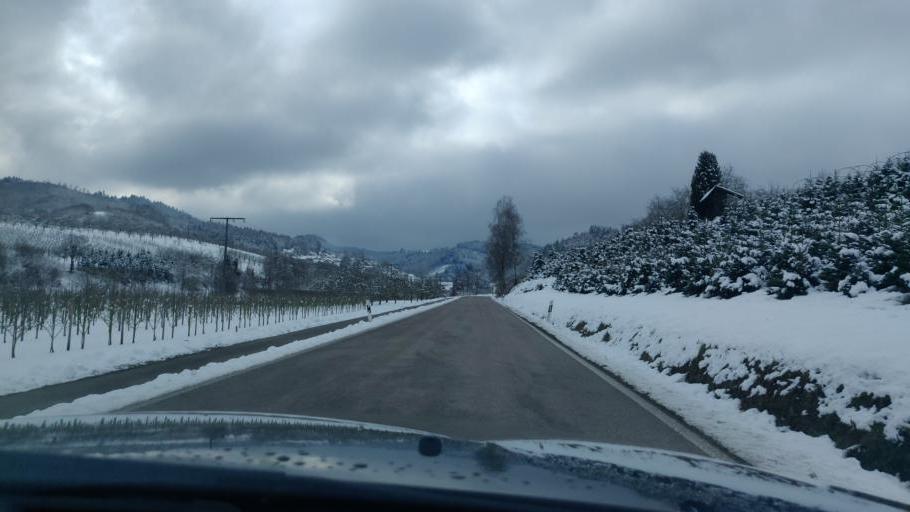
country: DE
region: Baden-Wuerttemberg
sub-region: Freiburg Region
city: Lautenbach
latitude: 48.5062
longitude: 8.0928
